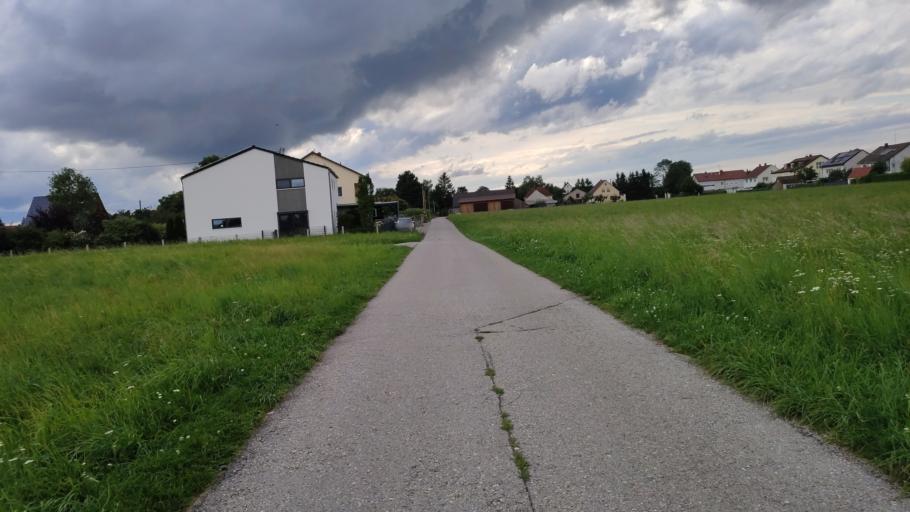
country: DE
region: Bavaria
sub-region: Swabia
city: Konigsbrunn
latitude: 48.2539
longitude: 10.8855
